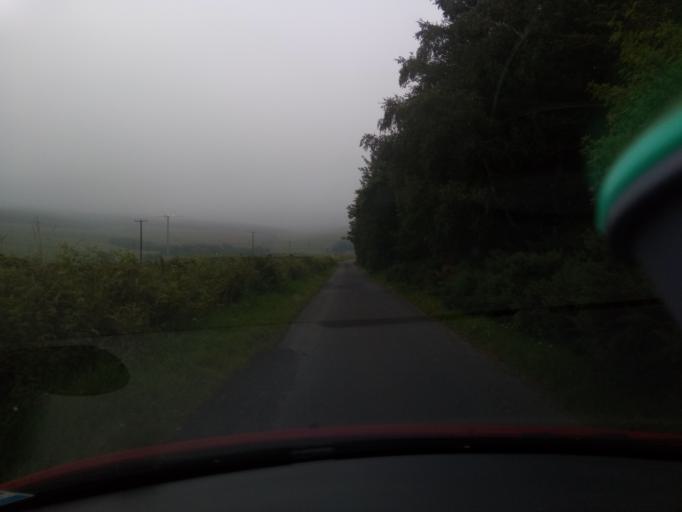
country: GB
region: Scotland
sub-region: The Scottish Borders
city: Galashiels
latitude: 55.6476
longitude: -2.7605
